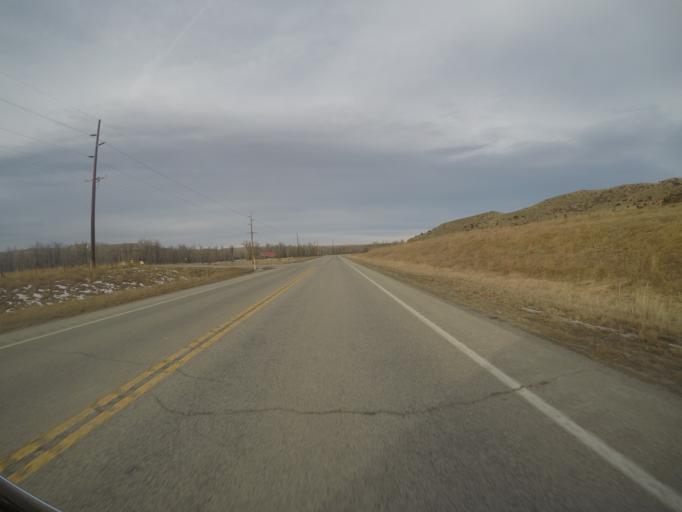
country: US
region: Montana
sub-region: Stillwater County
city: Absarokee
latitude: 45.4859
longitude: -109.4522
